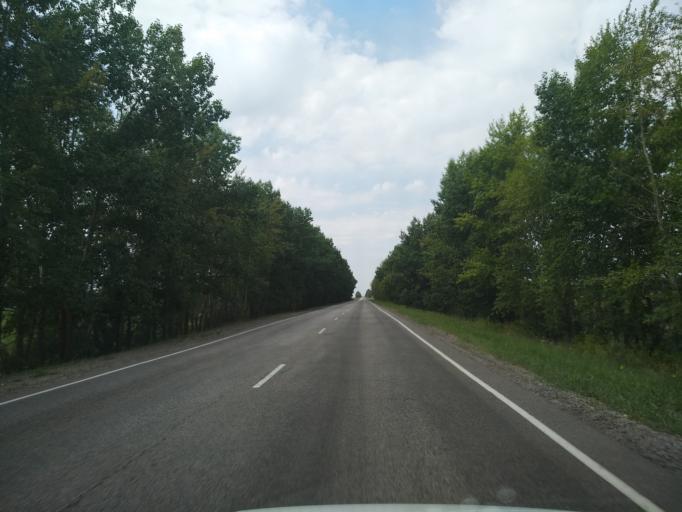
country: RU
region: Voronezj
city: Pereleshino
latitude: 51.7279
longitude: 40.0511
